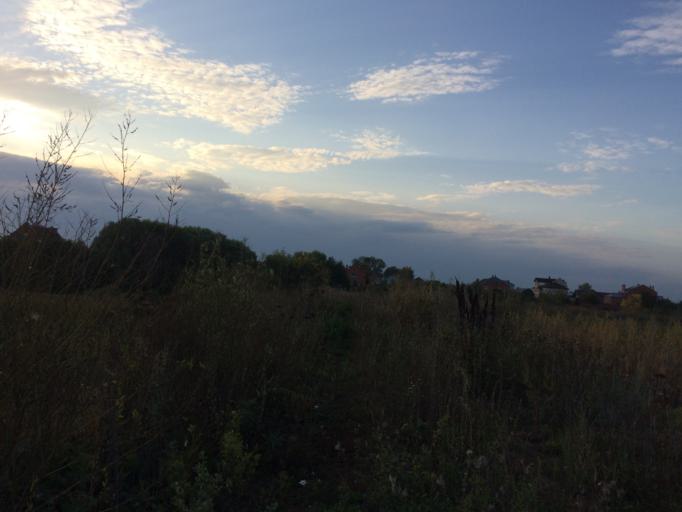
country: RU
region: Mariy-El
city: Yoshkar-Ola
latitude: 56.6483
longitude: 47.9218
